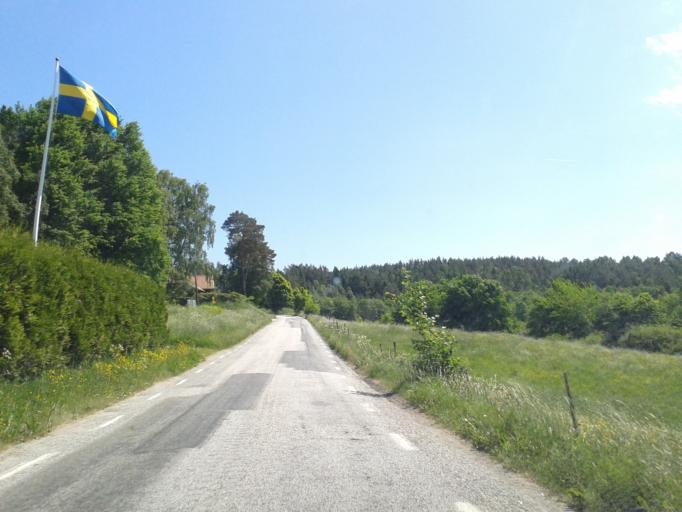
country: SE
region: Vaestra Goetaland
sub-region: Stenungsunds Kommun
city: Stora Hoga
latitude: 58.0206
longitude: 11.8836
